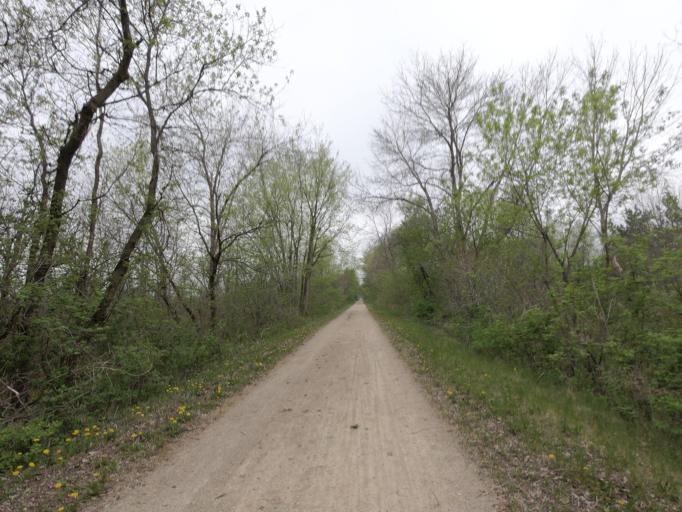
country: US
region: Wisconsin
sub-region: Jefferson County
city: Johnson Creek
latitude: 43.0288
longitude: -88.7415
